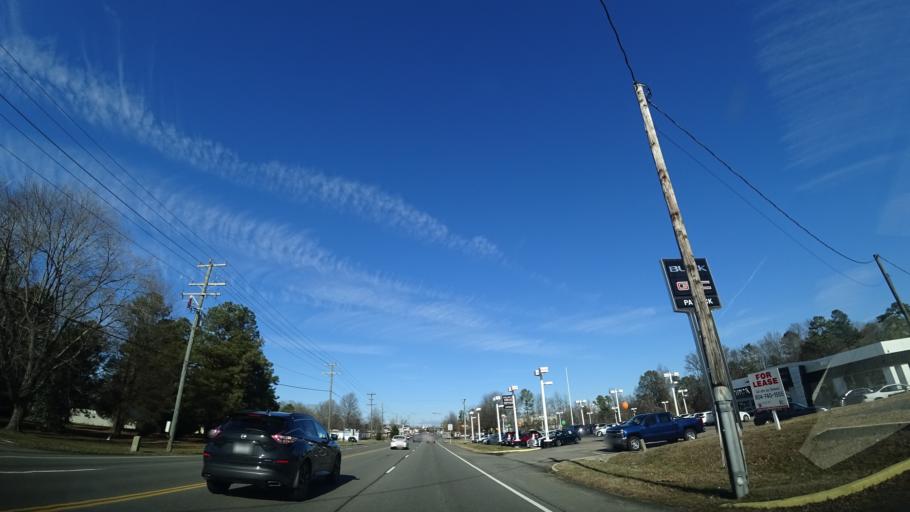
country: US
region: Virginia
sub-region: Hanover County
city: Ashland
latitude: 37.7509
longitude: -77.4713
